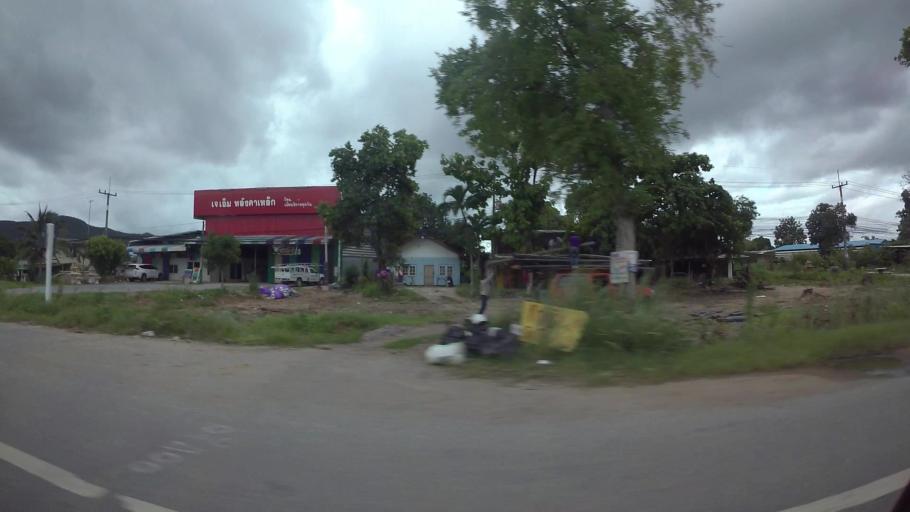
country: TH
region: Chon Buri
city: Sattahip
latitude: 12.7288
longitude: 100.8936
